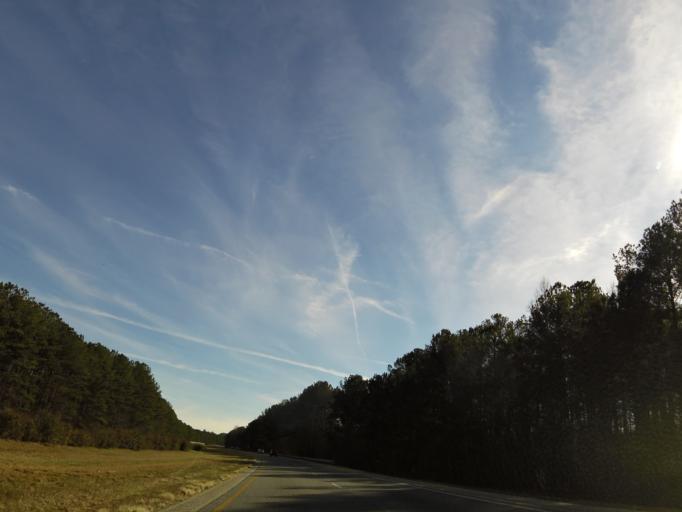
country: US
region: Georgia
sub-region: Troup County
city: La Grange
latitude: 32.9997
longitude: -84.9541
